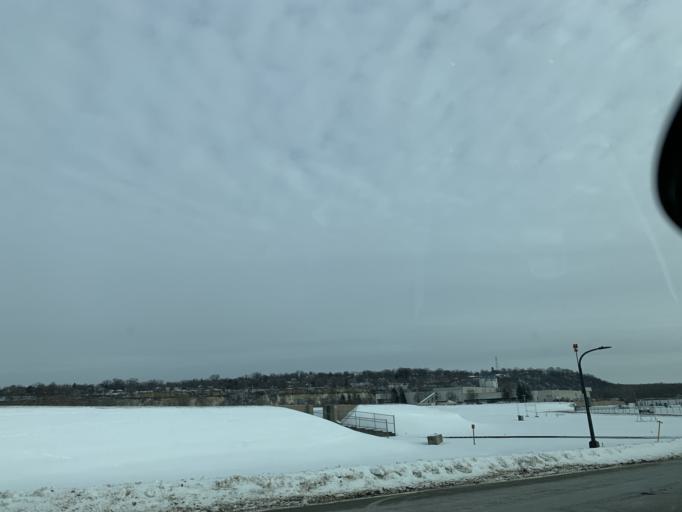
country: US
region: Minnesota
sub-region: Ramsey County
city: Saint Paul
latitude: 44.9422
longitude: -93.0710
